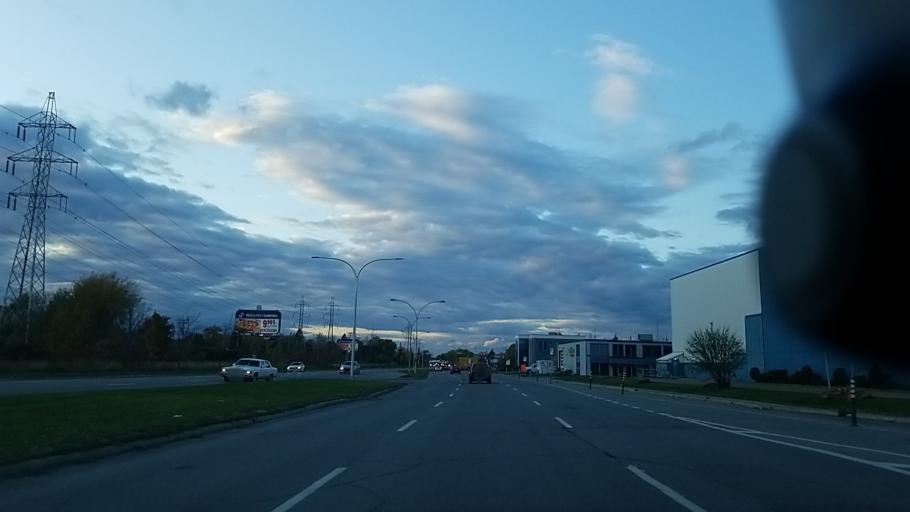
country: CA
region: Quebec
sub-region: Laval
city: Laval
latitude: 45.5726
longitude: -73.7220
